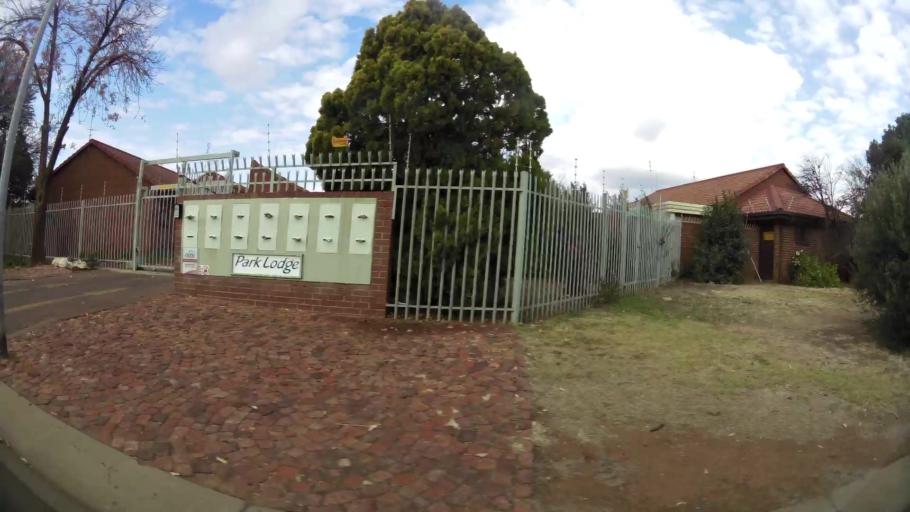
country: ZA
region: Orange Free State
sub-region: Mangaung Metropolitan Municipality
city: Bloemfontein
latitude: -29.0761
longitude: 26.1942
